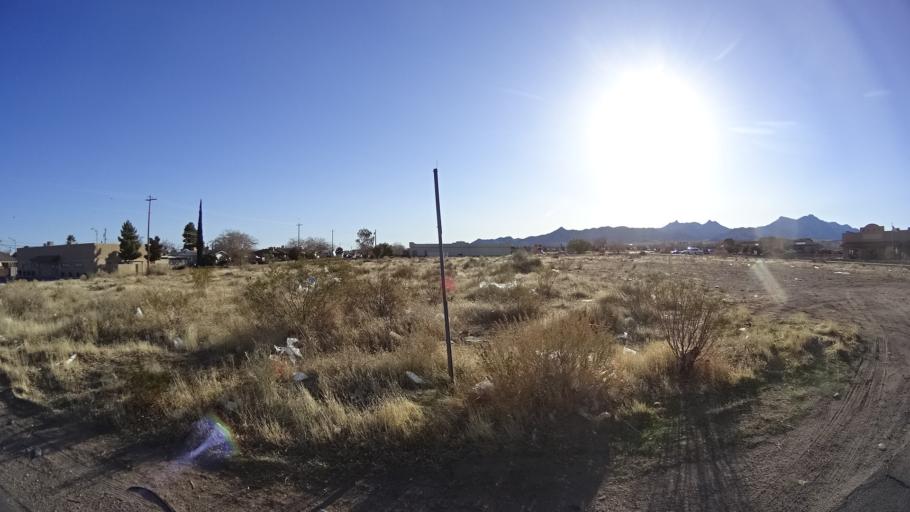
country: US
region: Arizona
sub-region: Mohave County
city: Kingman
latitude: 35.1918
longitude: -114.0181
